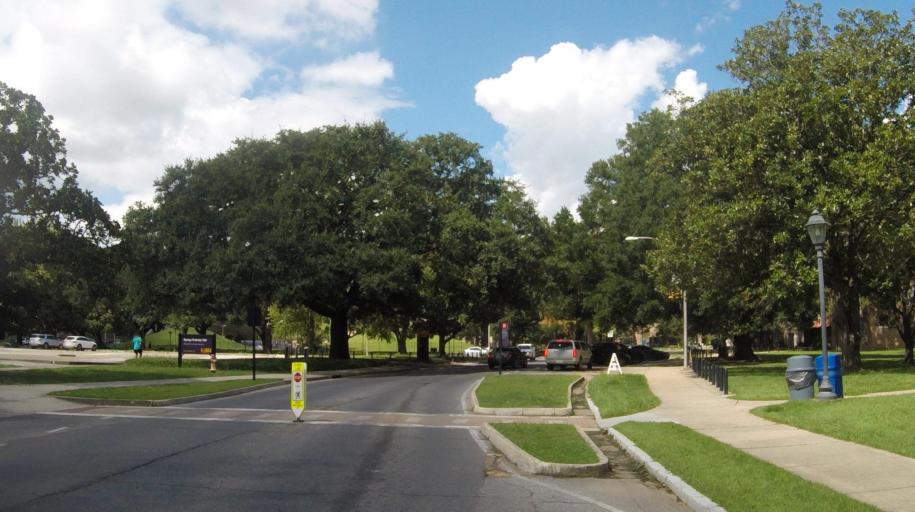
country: US
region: Louisiana
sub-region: East Baton Rouge Parish
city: Baton Rouge
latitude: 30.4158
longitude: -91.1805
